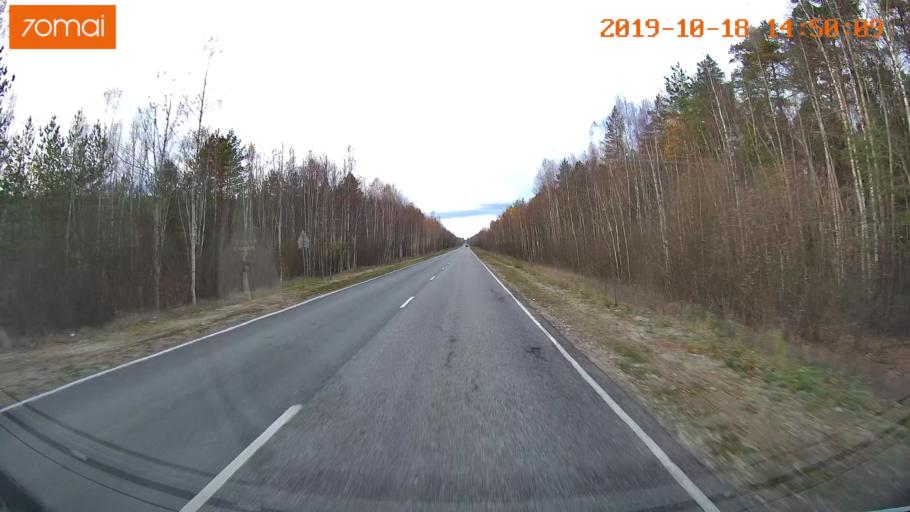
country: RU
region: Vladimir
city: Kurlovo
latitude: 55.4232
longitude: 40.6454
